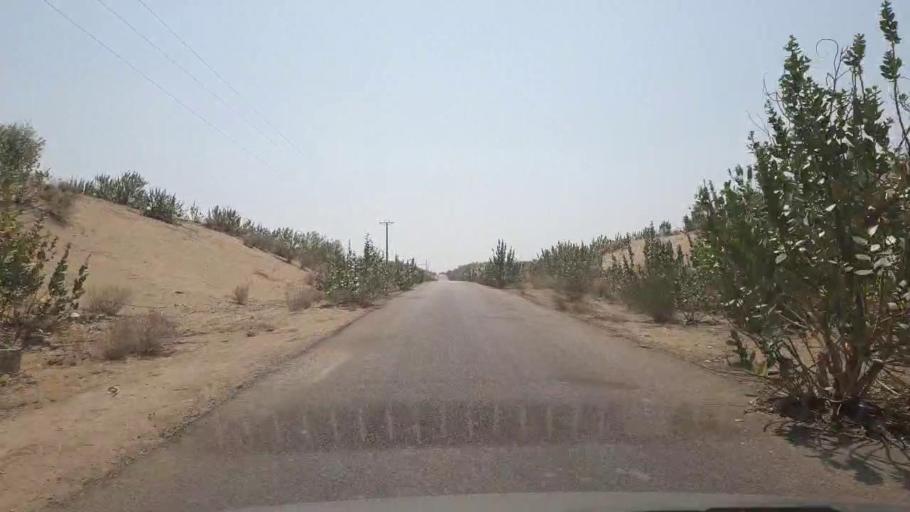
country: PK
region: Sindh
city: Chor
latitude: 25.6238
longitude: 70.1752
